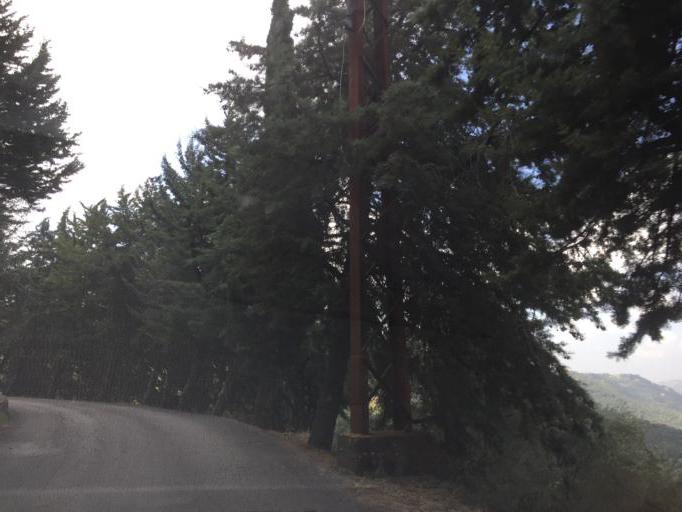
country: LB
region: Mont-Liban
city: Beit ed Dine
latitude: 33.6966
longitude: 35.5788
